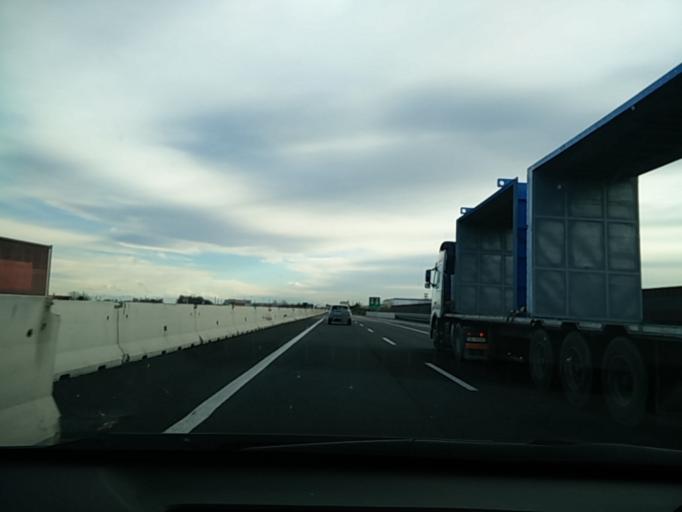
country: IT
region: Veneto
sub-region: Provincia di Venezia
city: Noventa di Piave
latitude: 45.6762
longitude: 12.5415
